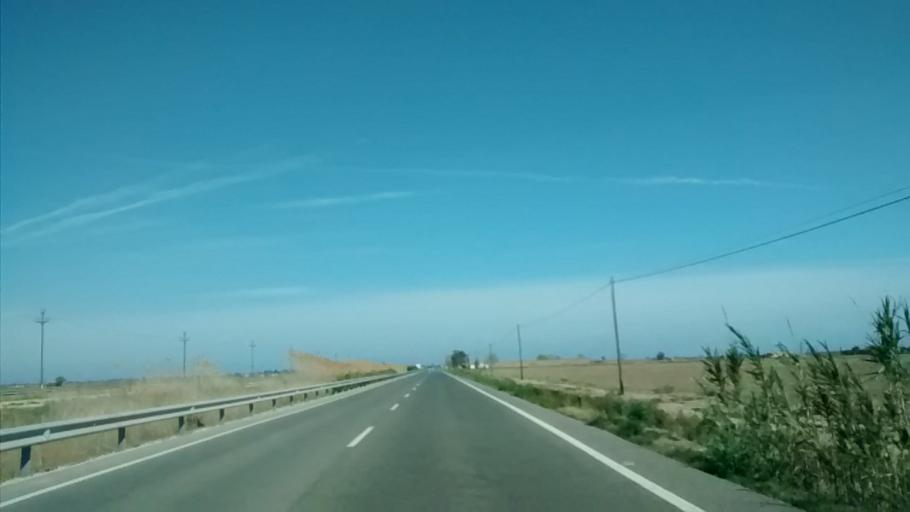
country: ES
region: Catalonia
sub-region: Provincia de Tarragona
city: Deltebre
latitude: 40.7057
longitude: 0.7772
